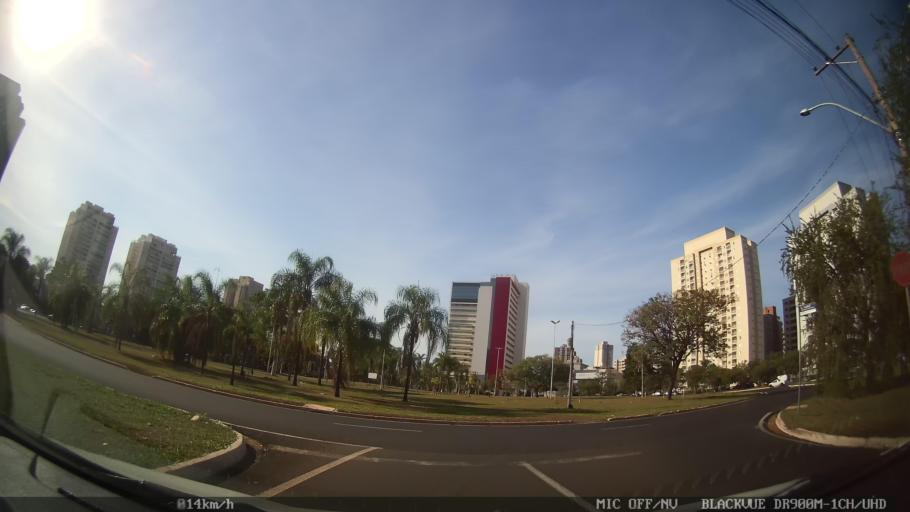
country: BR
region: Sao Paulo
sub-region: Ribeirao Preto
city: Ribeirao Preto
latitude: -21.2155
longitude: -47.8229
